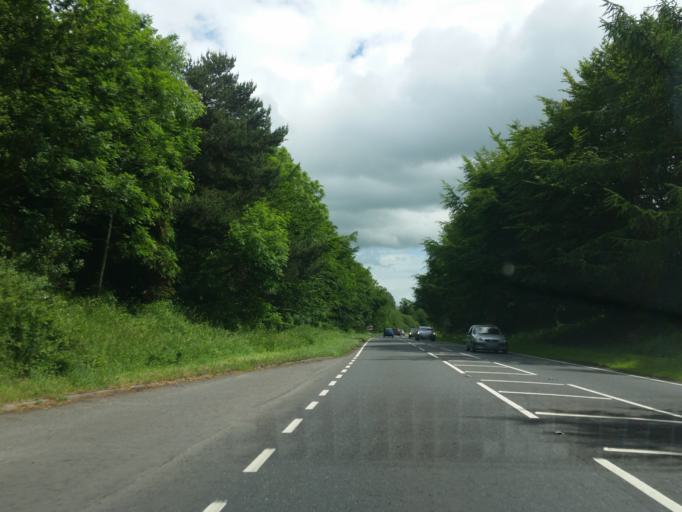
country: IE
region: Ulster
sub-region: County Monaghan
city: Monaghan
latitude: 54.4719
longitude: -7.0522
